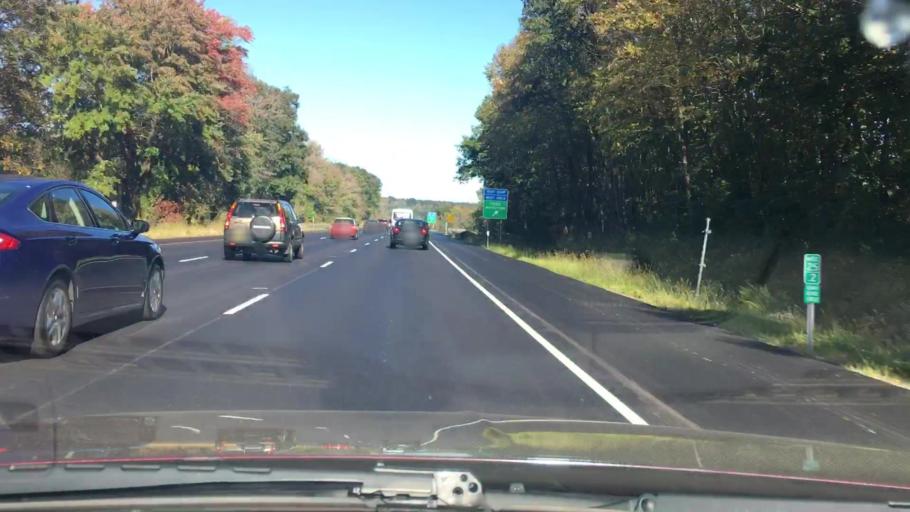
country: US
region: New York
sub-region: Putnam County
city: Brewster
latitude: 41.3587
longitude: -73.6361
